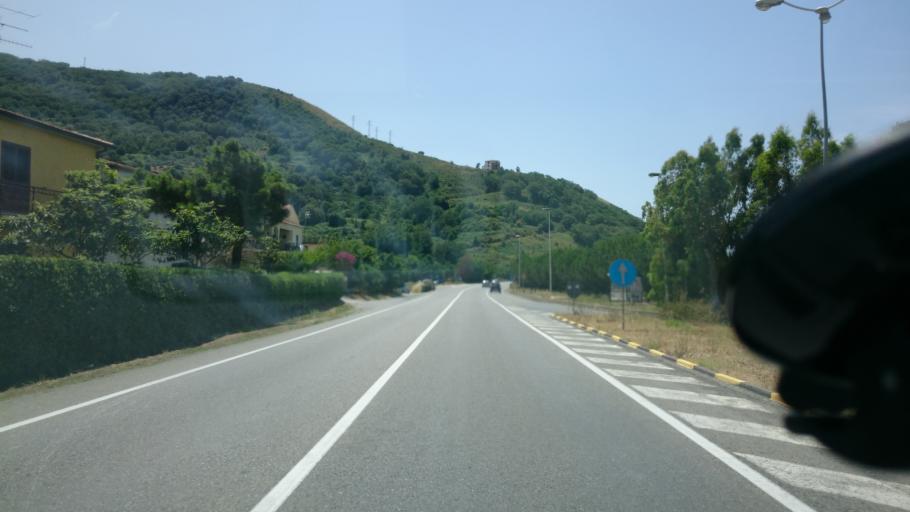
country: IT
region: Calabria
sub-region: Provincia di Cosenza
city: Cittadella del Capo
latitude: 39.5894
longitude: 15.8690
